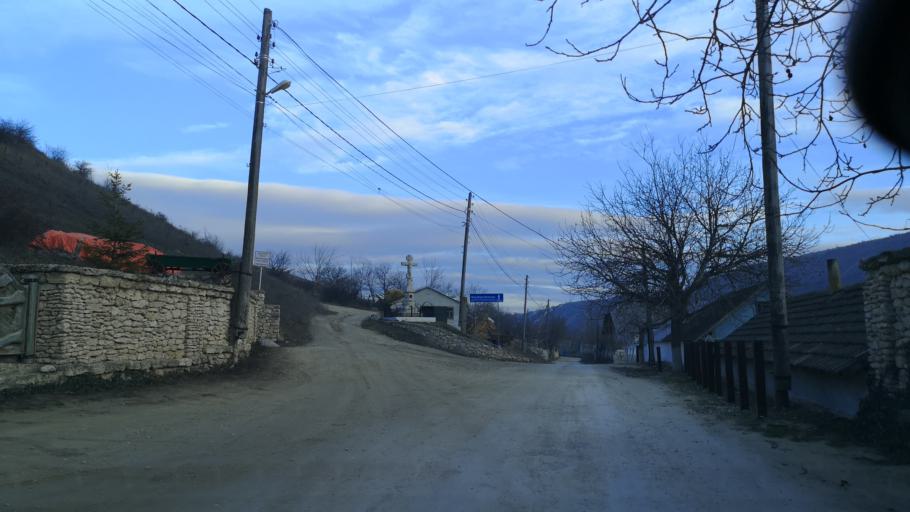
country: MD
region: Telenesti
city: Cocieri
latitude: 47.3004
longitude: 28.9710
